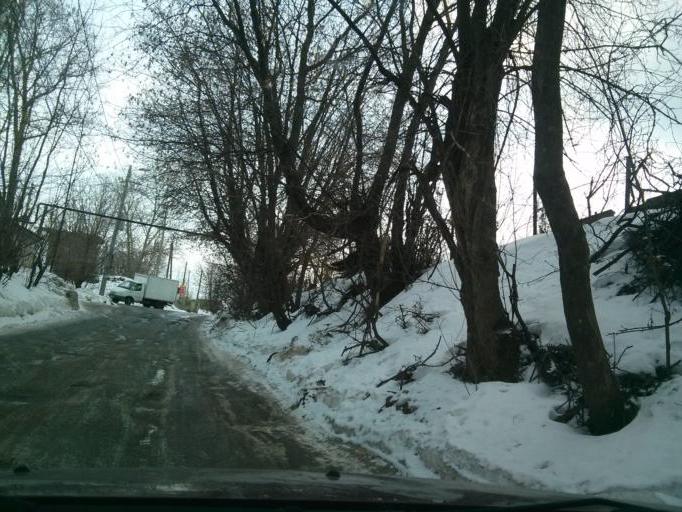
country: RU
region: Nizjnij Novgorod
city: Nizhniy Novgorod
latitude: 56.2736
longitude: 44.0328
